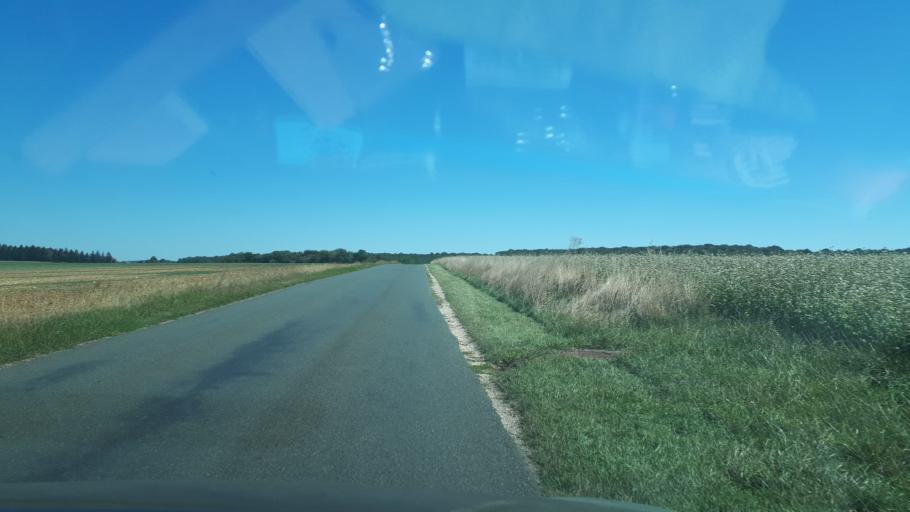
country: FR
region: Centre
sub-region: Departement du Cher
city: Rians
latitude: 47.1863
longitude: 2.6233
